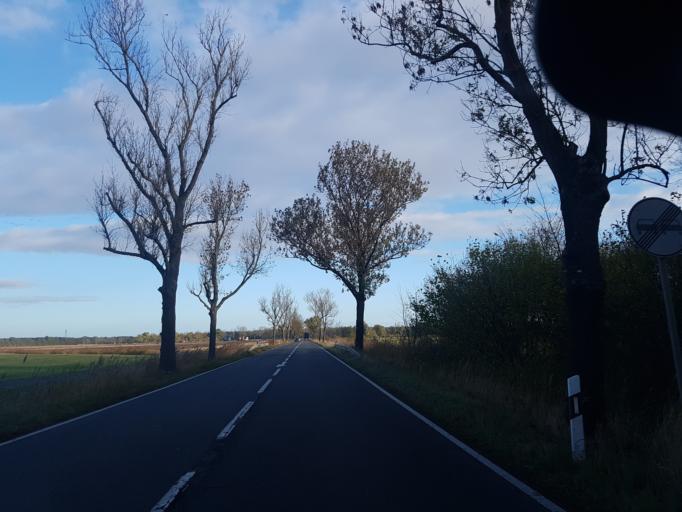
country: DE
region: Brandenburg
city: Nauen
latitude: 52.6436
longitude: 12.9247
